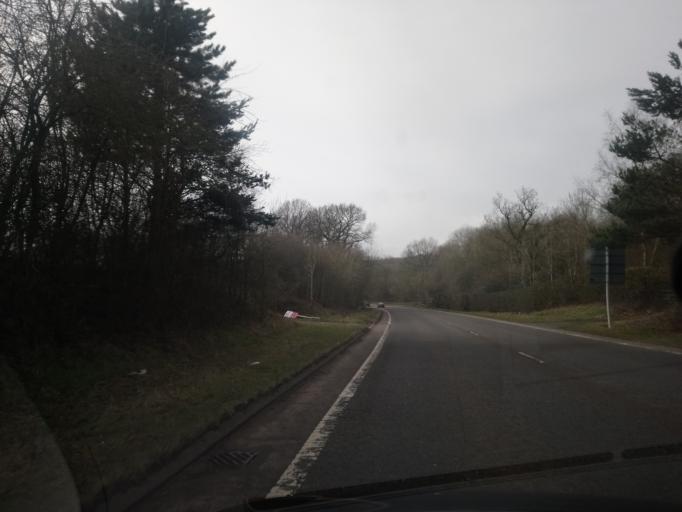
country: GB
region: England
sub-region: Telford and Wrekin
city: Ironbridge
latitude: 52.6522
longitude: -2.5007
